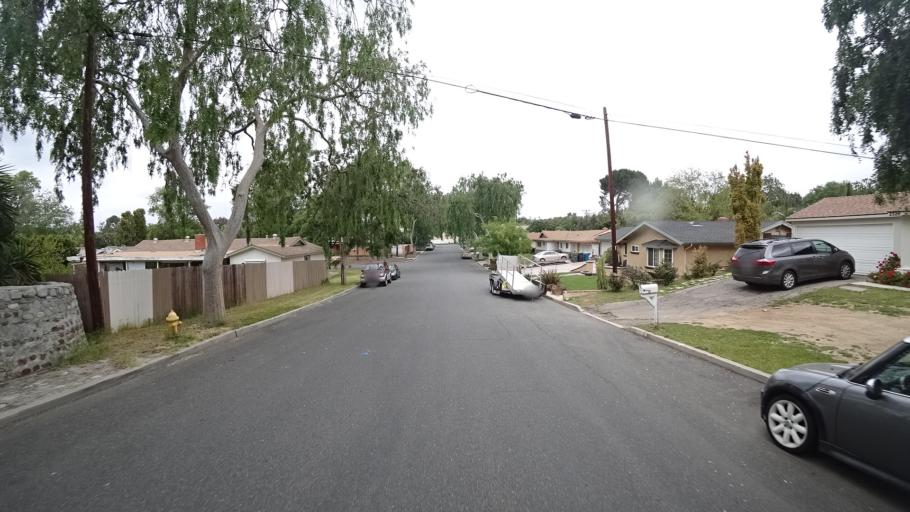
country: US
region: California
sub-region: Ventura County
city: Thousand Oaks
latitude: 34.2130
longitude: -118.8606
